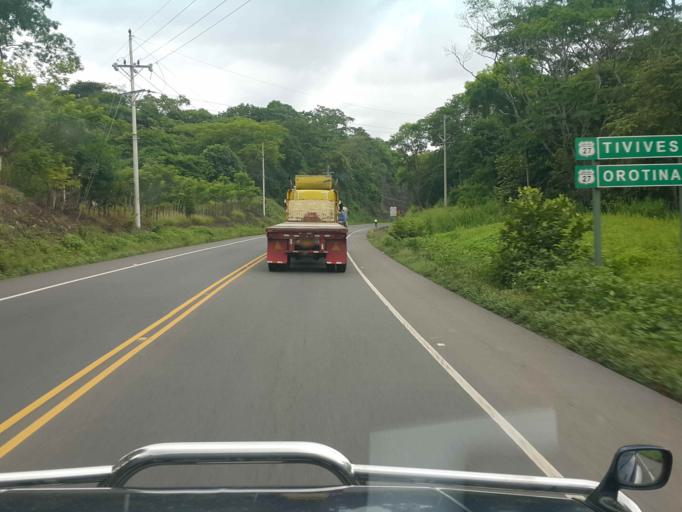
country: CR
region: Puntarenas
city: Esparza
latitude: 9.9196
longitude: -84.6865
